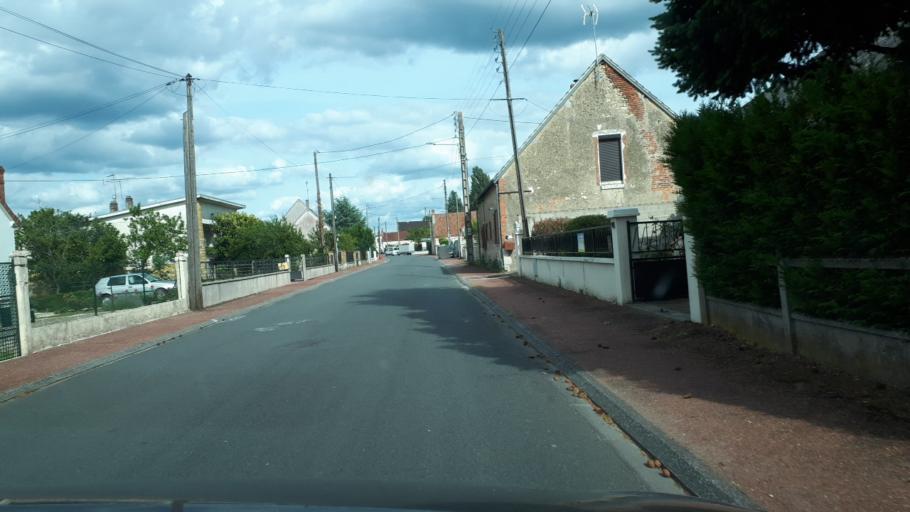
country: FR
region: Centre
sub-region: Departement du Loir-et-Cher
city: Romorantin-Lanthenay
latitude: 47.3521
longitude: 1.7555
